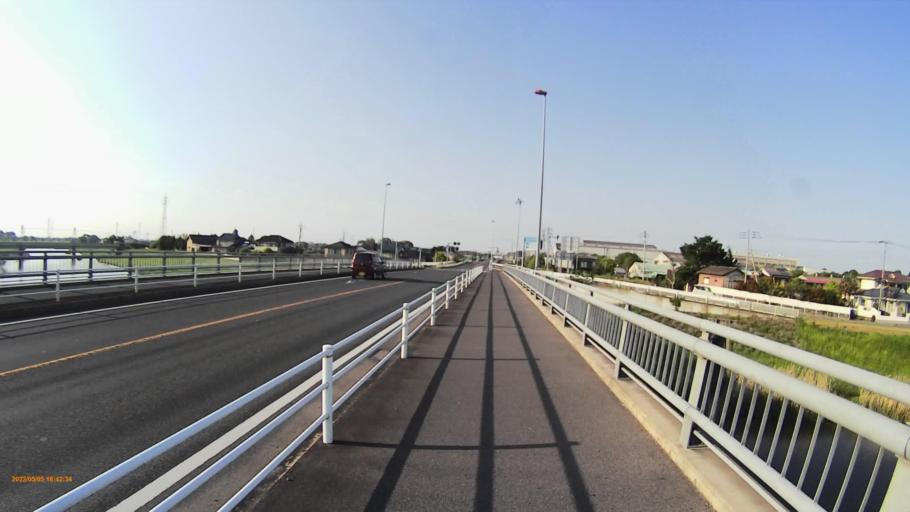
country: JP
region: Saitama
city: Satte
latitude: 36.0958
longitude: 139.7218
